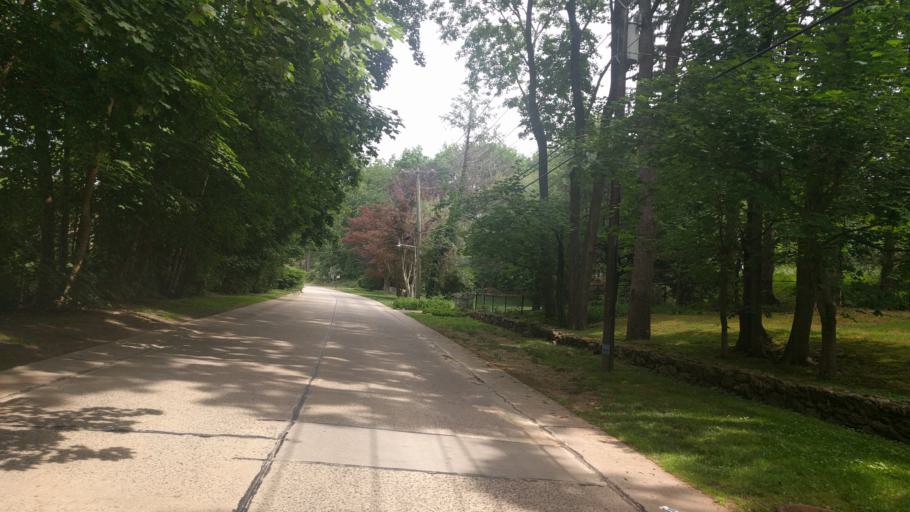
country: US
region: New York
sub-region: Nassau County
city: Roslyn Harbor
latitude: 40.8208
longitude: -73.6365
